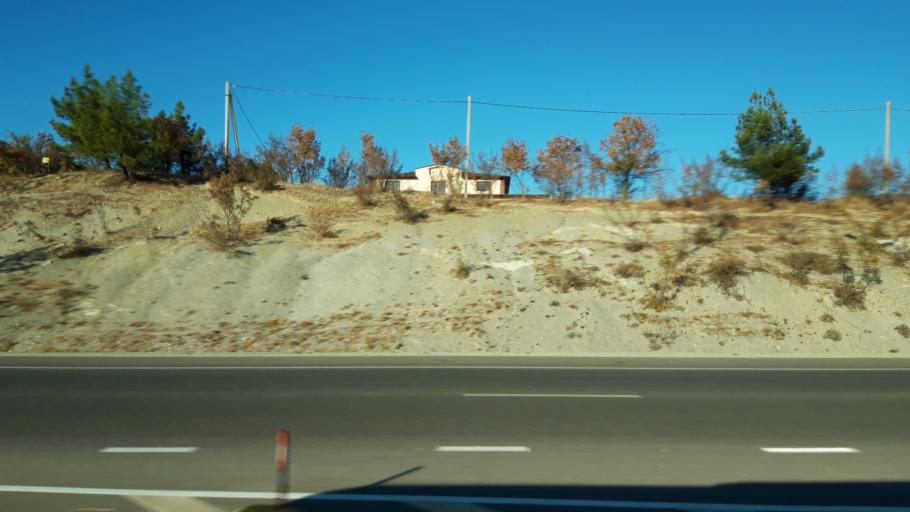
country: RU
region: Krasnodarskiy
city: Kabardinka
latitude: 44.6394
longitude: 37.9850
